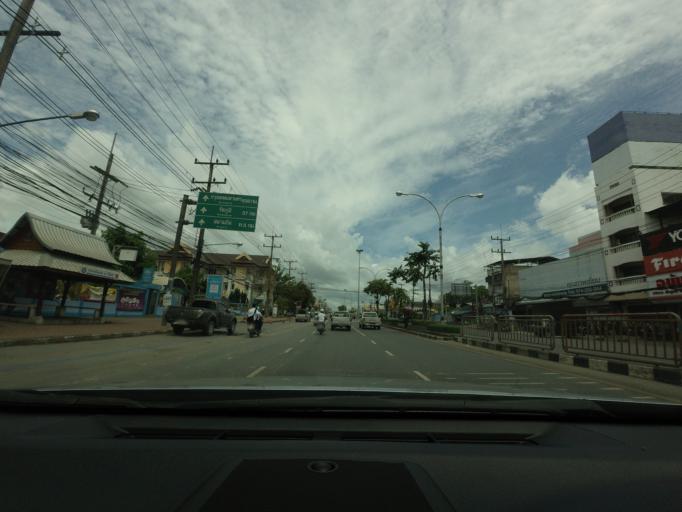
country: TH
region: Songkhla
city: Hat Yai
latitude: 7.0026
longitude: 100.4574
